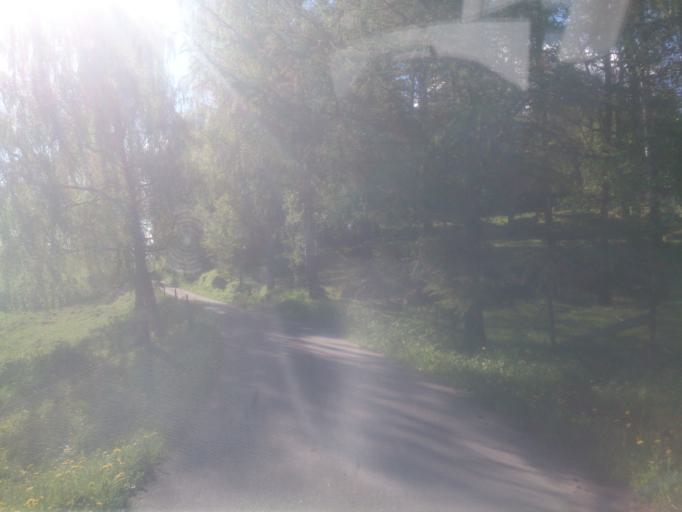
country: SE
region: OEstergoetland
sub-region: Atvidabergs Kommun
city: Atvidaberg
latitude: 58.2994
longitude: 16.0778
